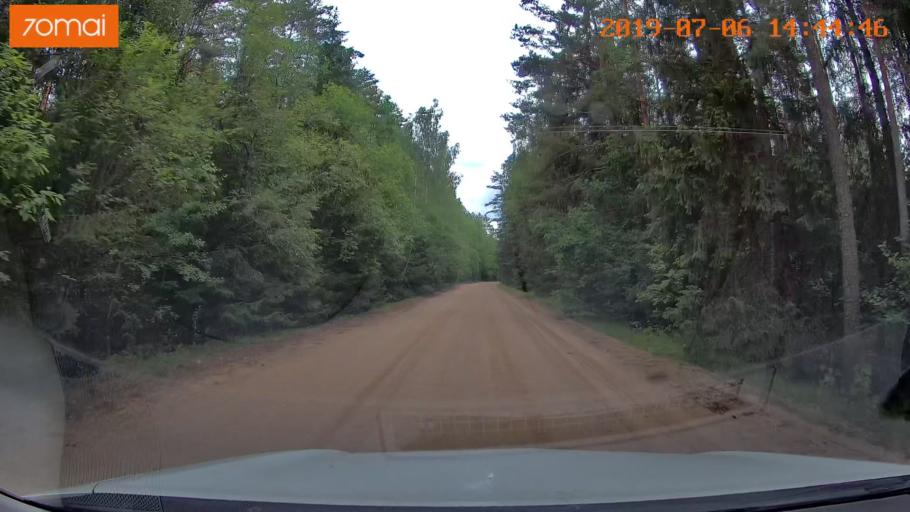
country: BY
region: Minsk
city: Ivyanyets
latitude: 53.9653
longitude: 26.6913
